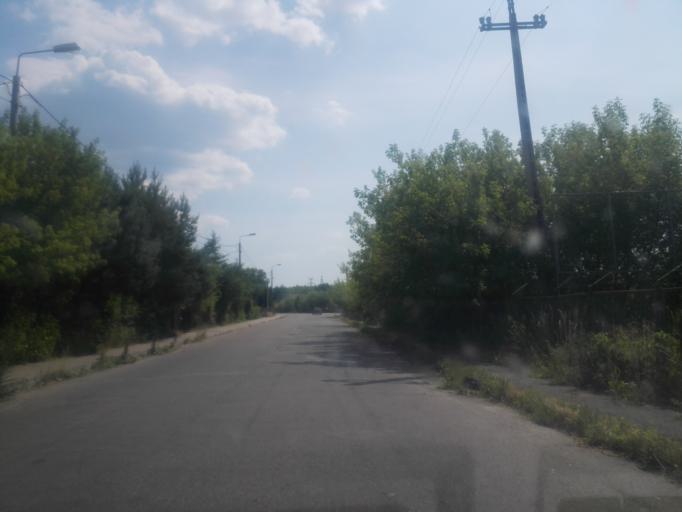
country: PL
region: Podlasie
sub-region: Suwalki
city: Suwalki
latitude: 54.0248
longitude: 22.9806
